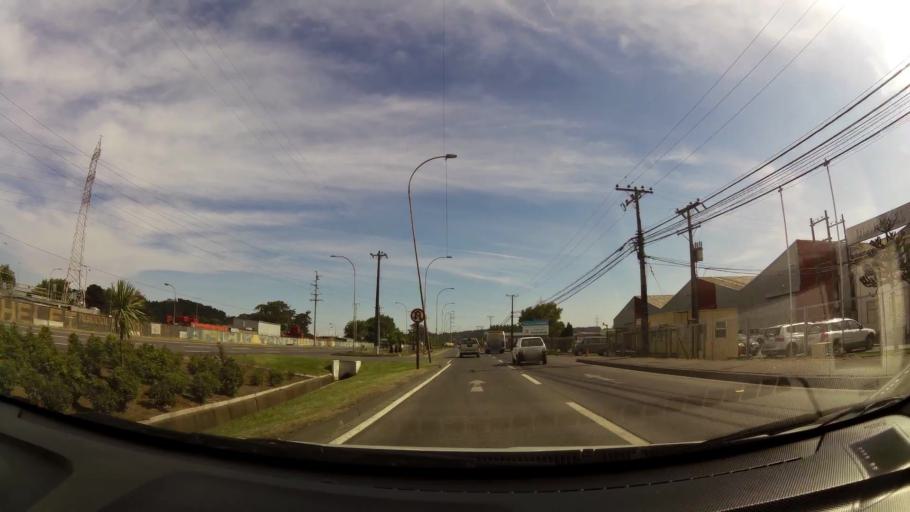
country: CL
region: Biobio
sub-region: Provincia de Concepcion
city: Talcahuano
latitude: -36.7741
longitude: -73.1137
